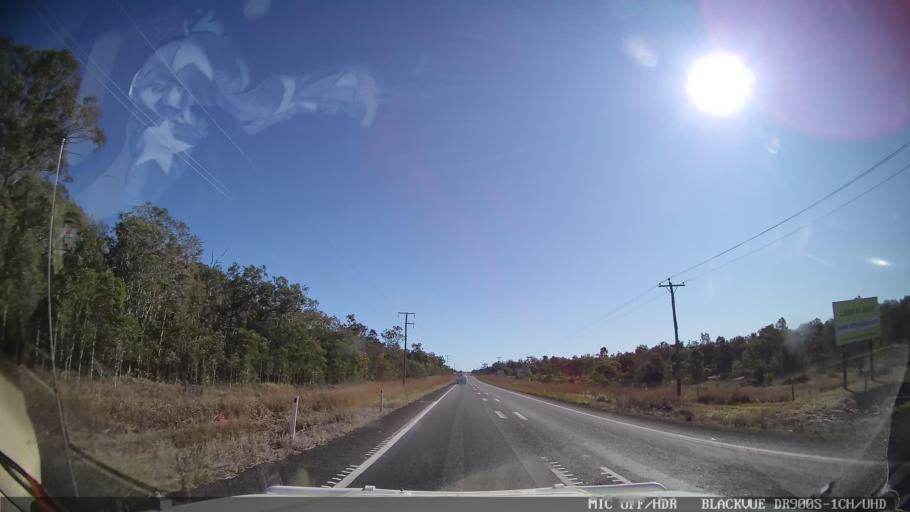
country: AU
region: Queensland
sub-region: Bundaberg
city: Childers
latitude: -25.2499
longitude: 152.3452
